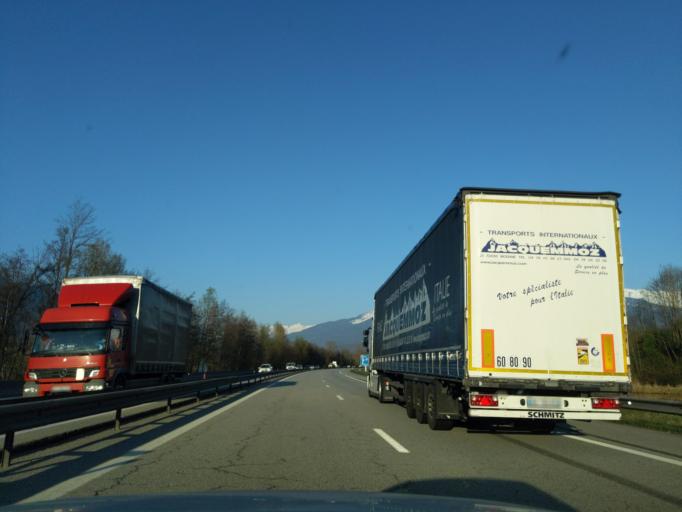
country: FR
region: Rhone-Alpes
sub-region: Departement de la Savoie
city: Coise-Saint-Jean-Pied-Gauthier
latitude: 45.5560
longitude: 6.1807
